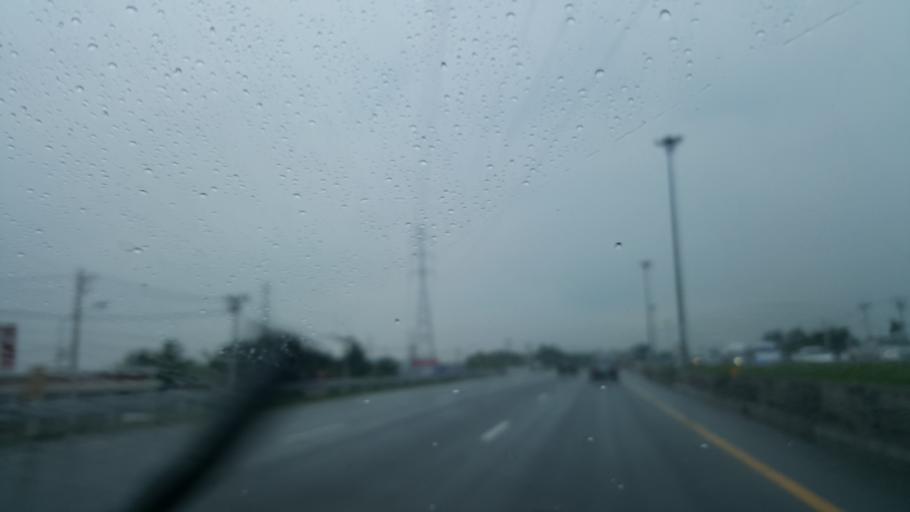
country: TH
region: Chon Buri
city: Ban Talat Bueng
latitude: 13.0662
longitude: 100.9957
